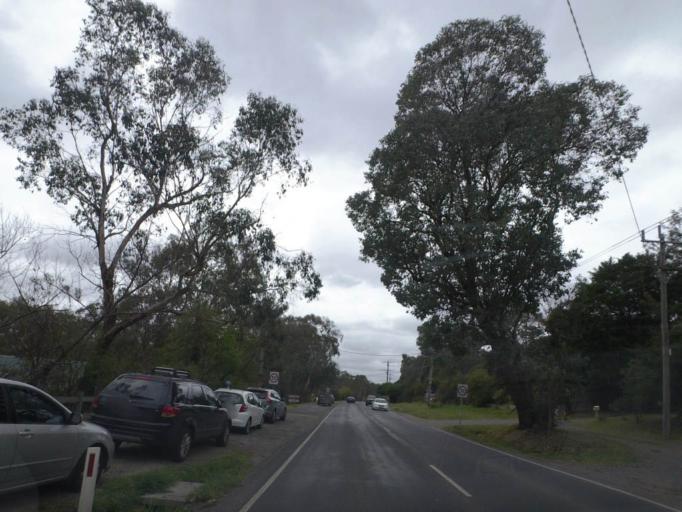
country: AU
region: Victoria
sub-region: Nillumbik
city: North Warrandyte
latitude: -37.7417
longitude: 145.2115
